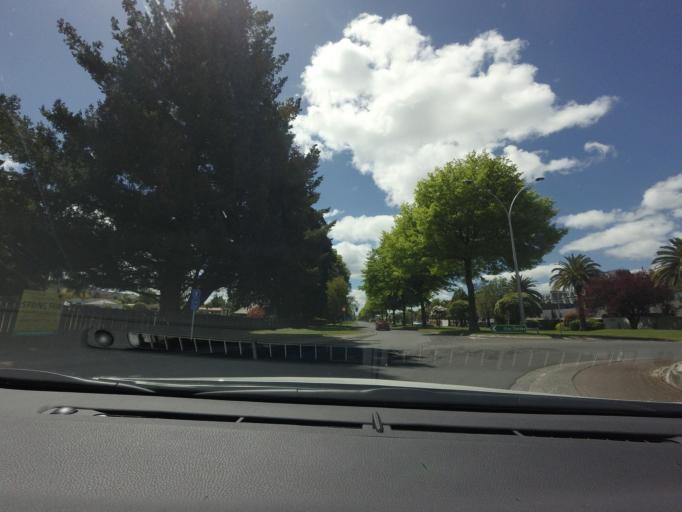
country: NZ
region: Bay of Plenty
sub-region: Rotorua District
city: Rotorua
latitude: -38.1587
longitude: 176.2536
